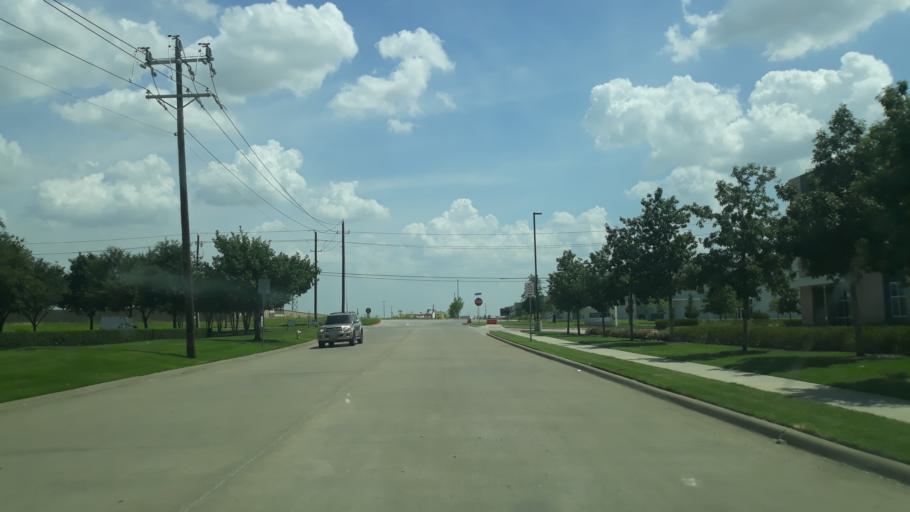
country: US
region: Texas
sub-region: Dallas County
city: Coppell
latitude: 32.9560
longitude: -97.0298
